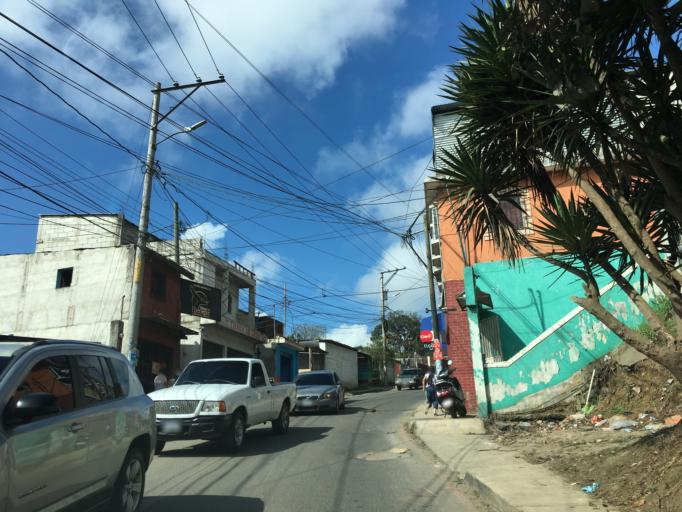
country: GT
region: Guatemala
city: San Jose Pinula
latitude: 14.5542
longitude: -90.4382
